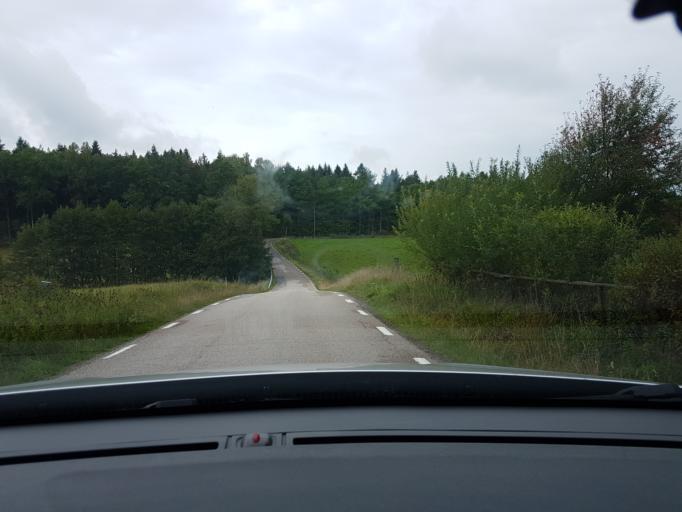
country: SE
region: Vaestra Goetaland
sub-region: Ale Kommun
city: Alvangen
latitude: 57.9079
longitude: 12.1645
